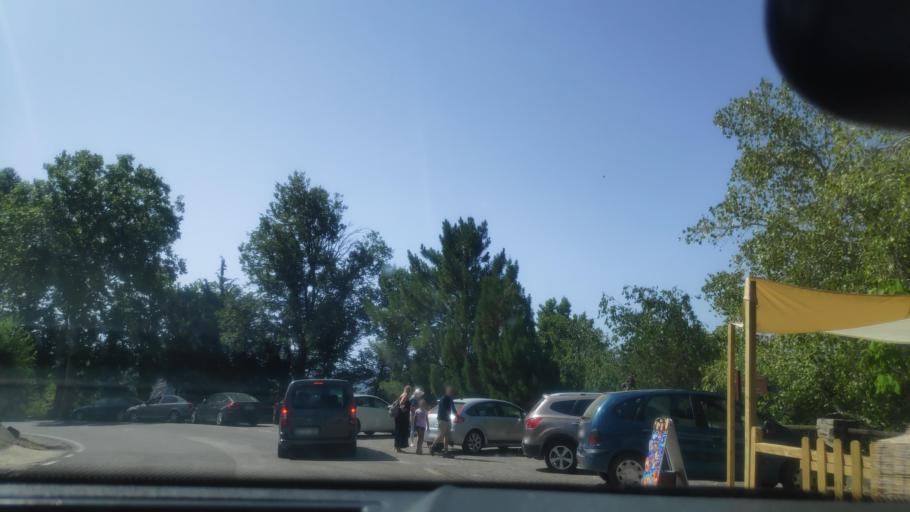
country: ES
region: Andalusia
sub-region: Provincia de Granada
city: Portugos
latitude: 36.9406
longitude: -3.3065
